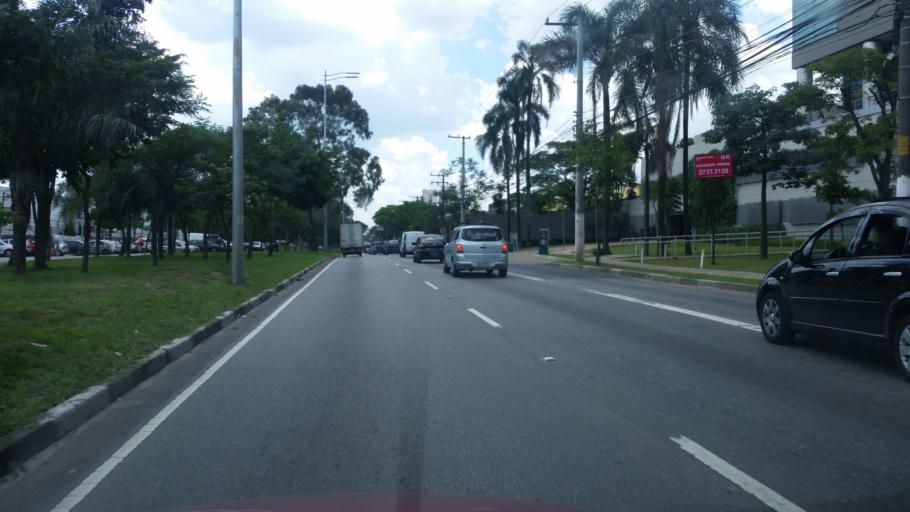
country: BR
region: Sao Paulo
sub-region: Diadema
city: Diadema
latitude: -23.6801
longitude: -46.6952
